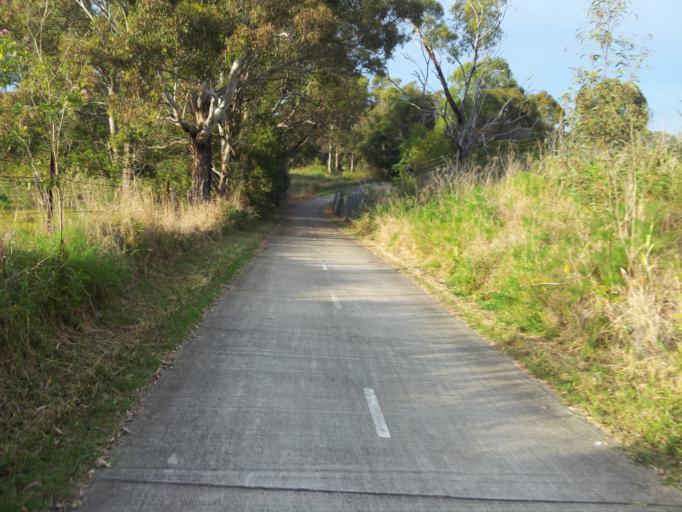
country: AU
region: New South Wales
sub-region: Fairfield
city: Horsley Park
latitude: -33.8385
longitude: 150.8764
